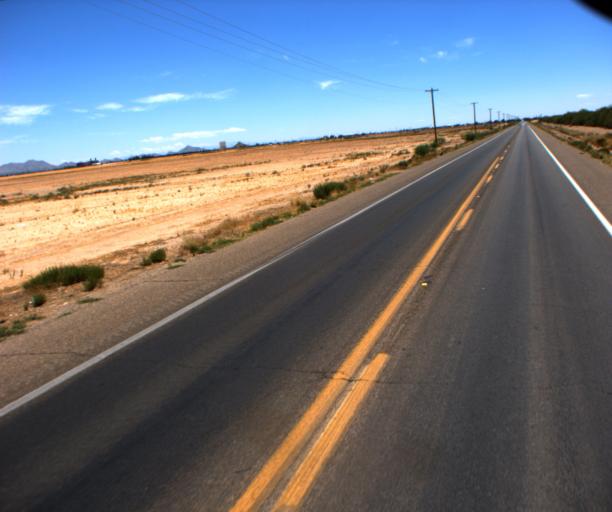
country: US
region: Arizona
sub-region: Pinal County
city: Casa Grande
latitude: 32.8794
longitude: -111.8249
